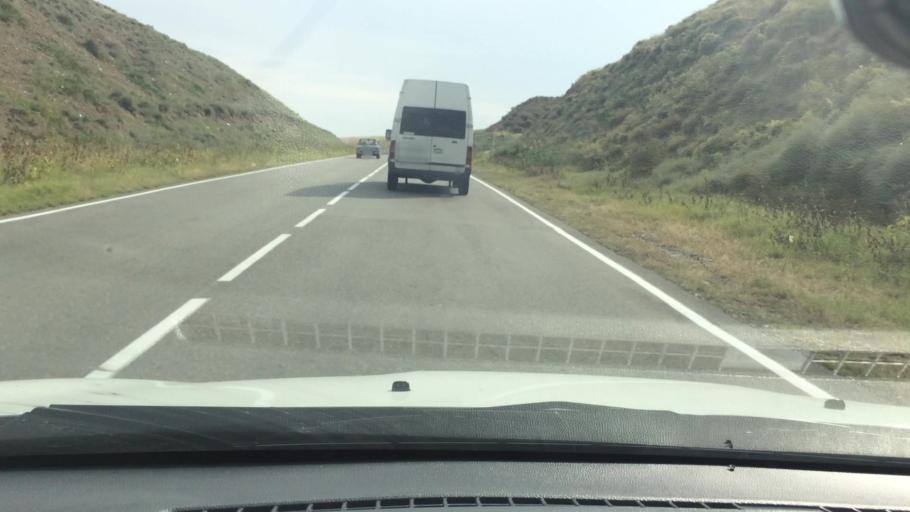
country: GE
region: Kvemo Kartli
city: Rust'avi
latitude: 41.5240
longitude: 44.9883
